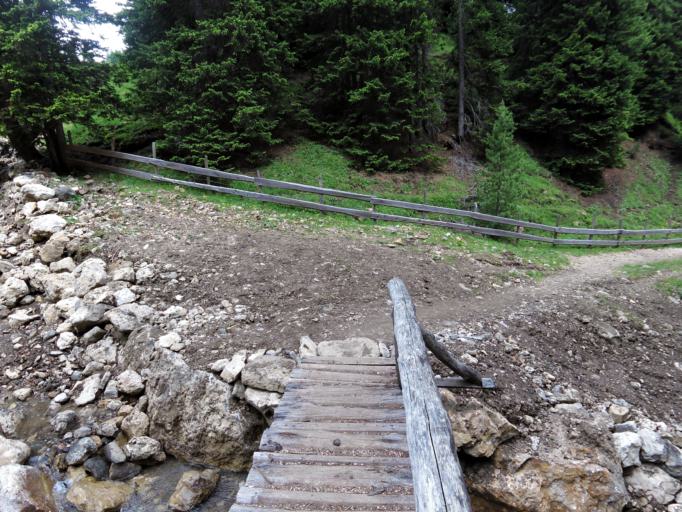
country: IT
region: Trentino-Alto Adige
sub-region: Bolzano
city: Ortisei
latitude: 46.5211
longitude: 11.6499
